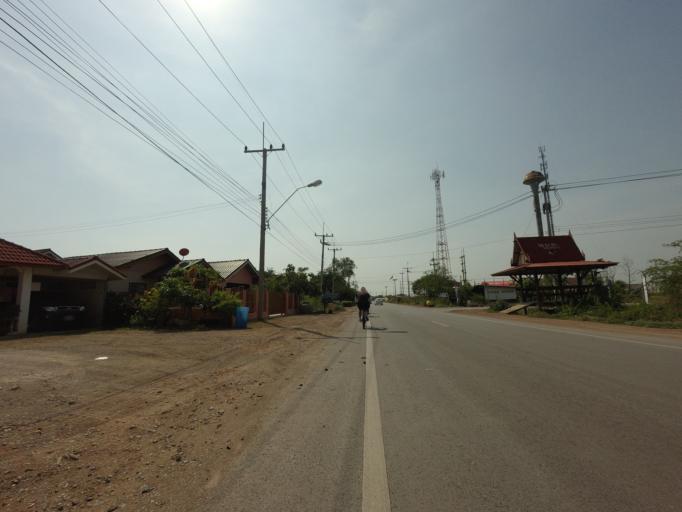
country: TH
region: Samut Sakhon
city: Samut Sakhon
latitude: 13.5174
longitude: 100.4037
